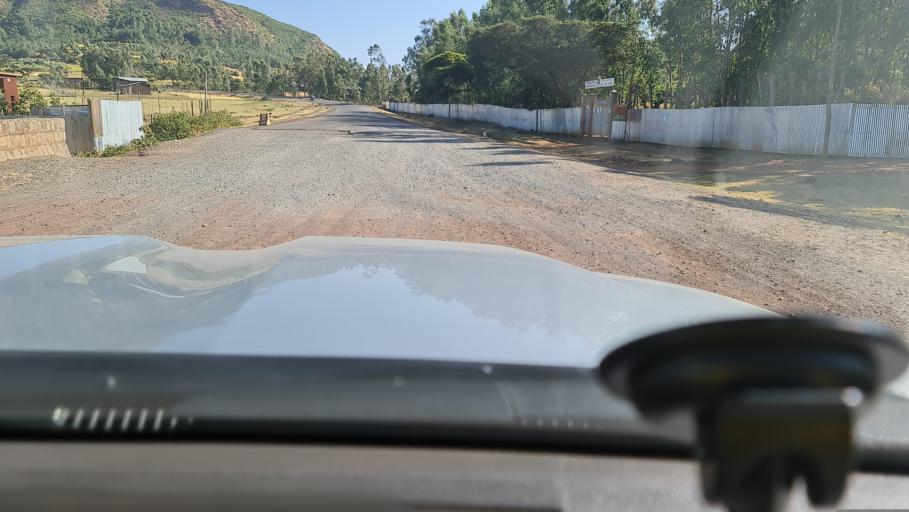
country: ET
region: Oromiya
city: Waliso
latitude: 8.6123
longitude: 37.9240
